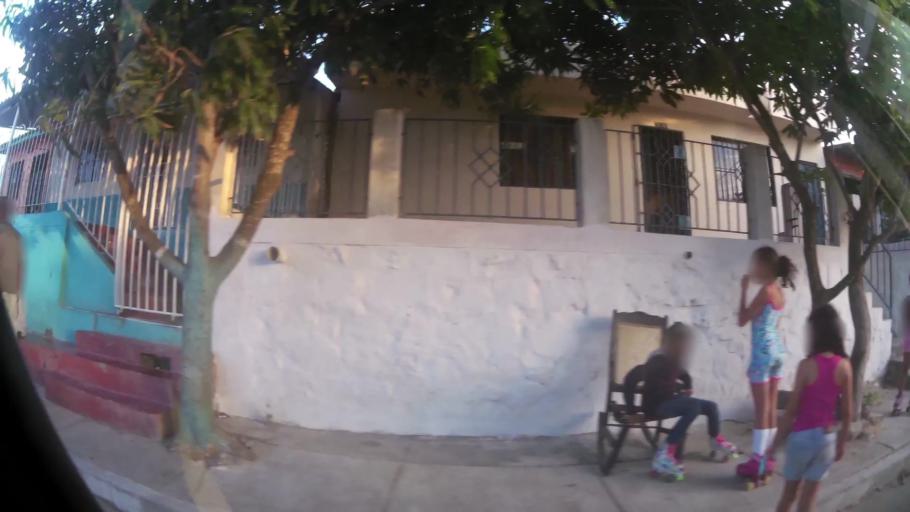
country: CO
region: Atlantico
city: Barranquilla
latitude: 10.9484
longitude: -74.8176
